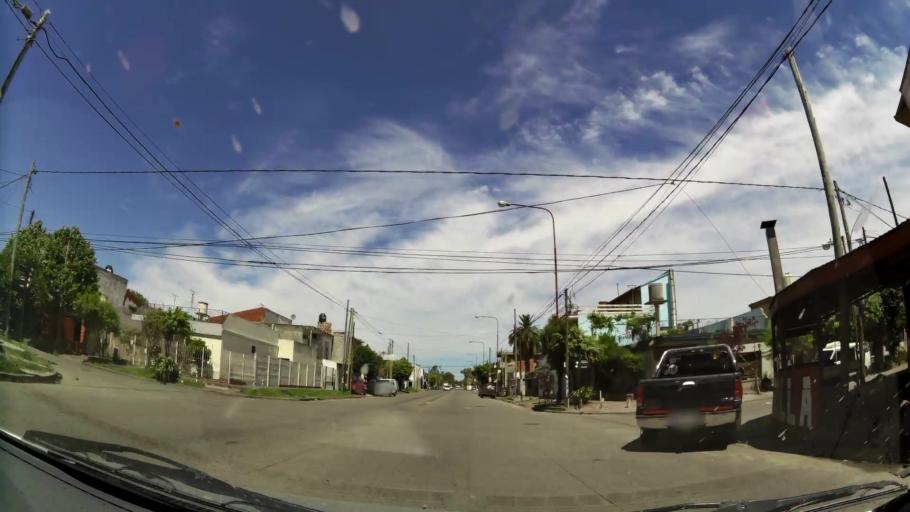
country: AR
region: Buenos Aires
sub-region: Partido de Quilmes
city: Quilmes
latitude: -34.7333
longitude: -58.3020
